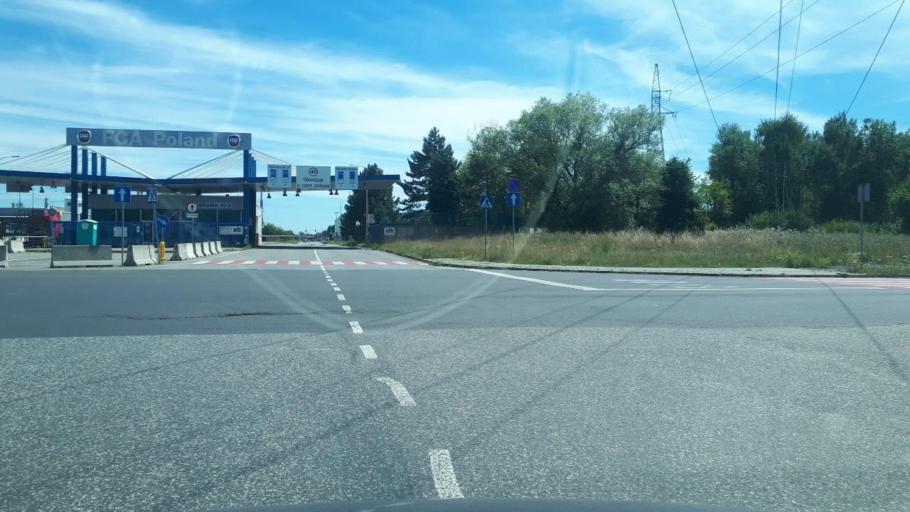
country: PL
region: Silesian Voivodeship
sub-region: Powiat bierunsko-ledzinski
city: Bierun
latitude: 50.1057
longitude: 19.0606
